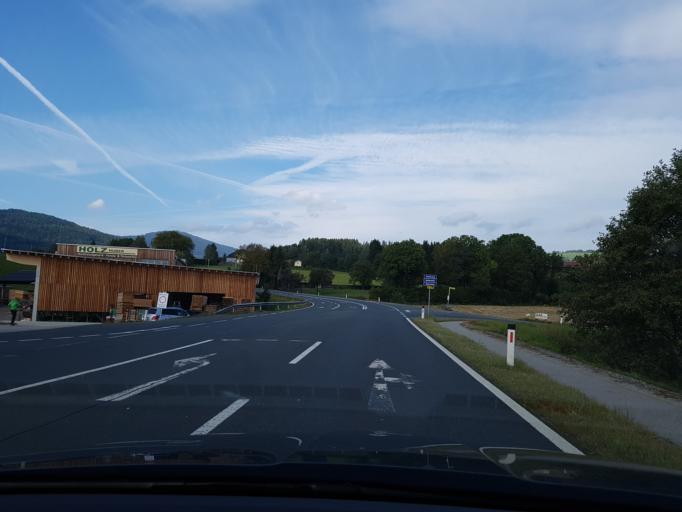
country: AT
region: Carinthia
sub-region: Politischer Bezirk Feldkirchen
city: Feldkirchen in Karnten
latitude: 46.7353
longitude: 14.0712
